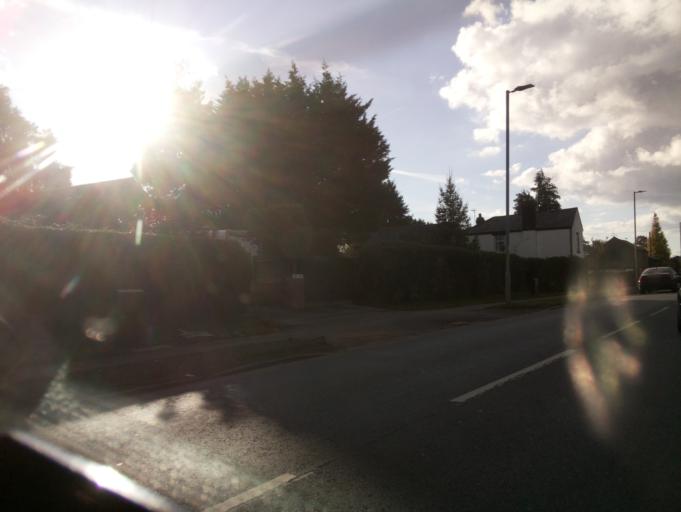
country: GB
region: England
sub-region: Herefordshire
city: Belmont
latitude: 52.0679
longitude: -2.7658
